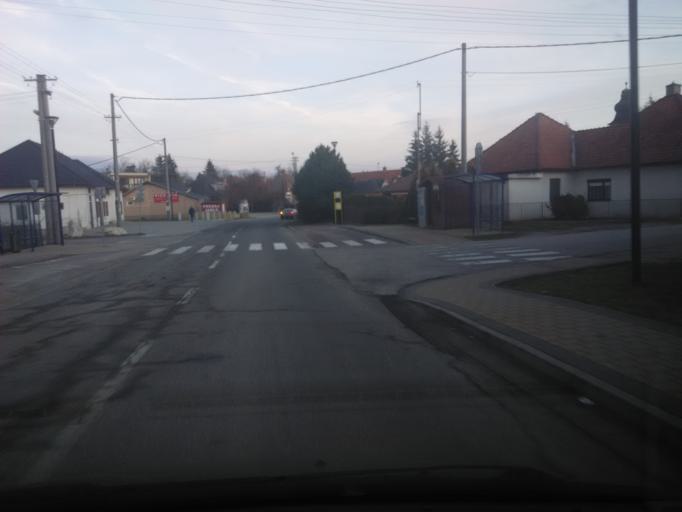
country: SK
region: Nitriansky
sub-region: Okres Nitra
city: Nitra
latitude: 48.3798
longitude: 18.2229
